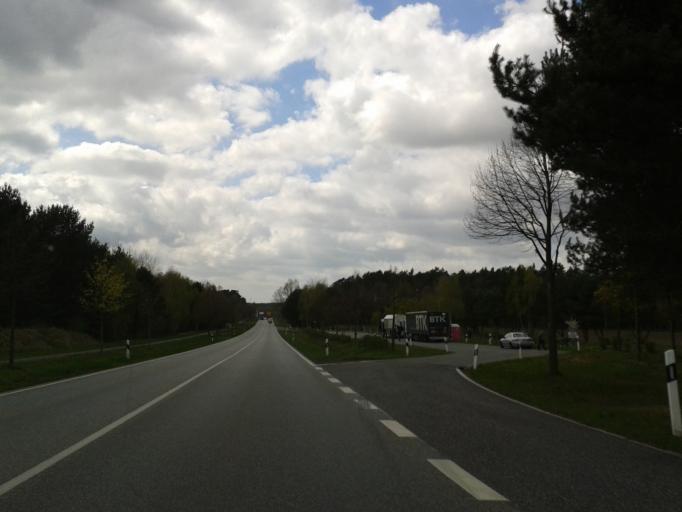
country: DE
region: Lower Saxony
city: Bergen an der Dumme
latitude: 52.8841
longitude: 11.0004
